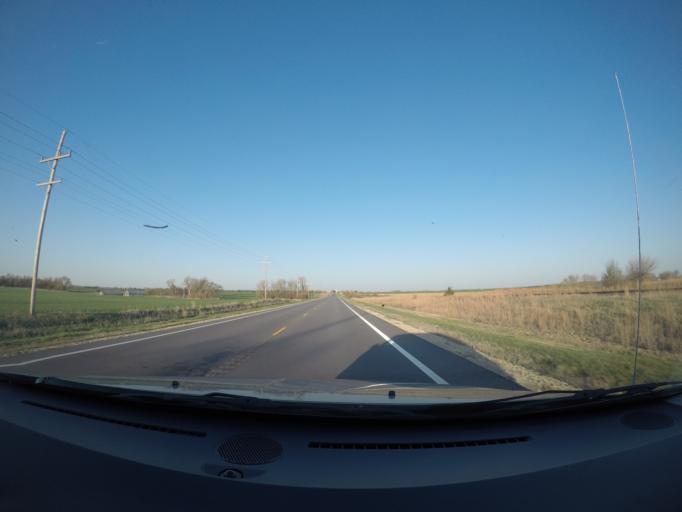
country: US
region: Kansas
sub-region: Stafford County
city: Stafford
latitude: 37.8194
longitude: -98.4087
